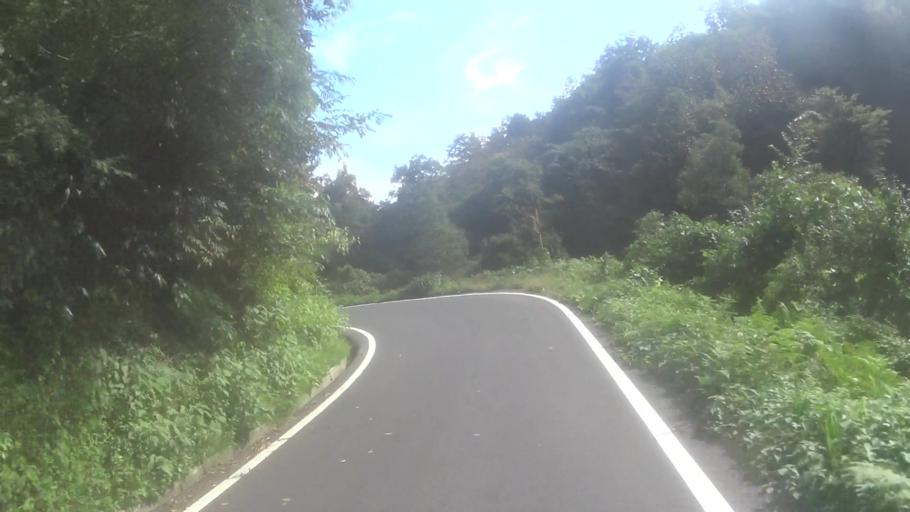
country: JP
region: Kyoto
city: Miyazu
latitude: 35.6122
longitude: 135.1207
